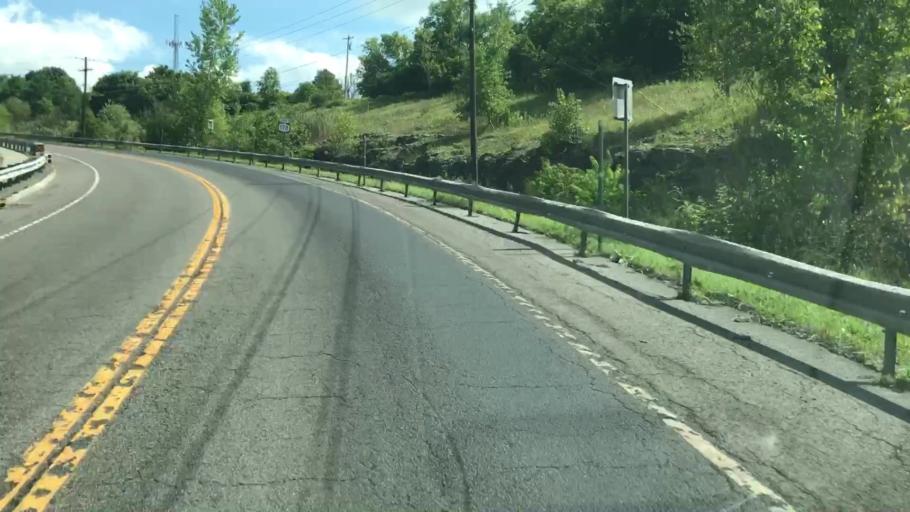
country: US
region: New York
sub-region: Onondaga County
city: Nedrow
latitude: 42.9902
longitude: -76.0684
